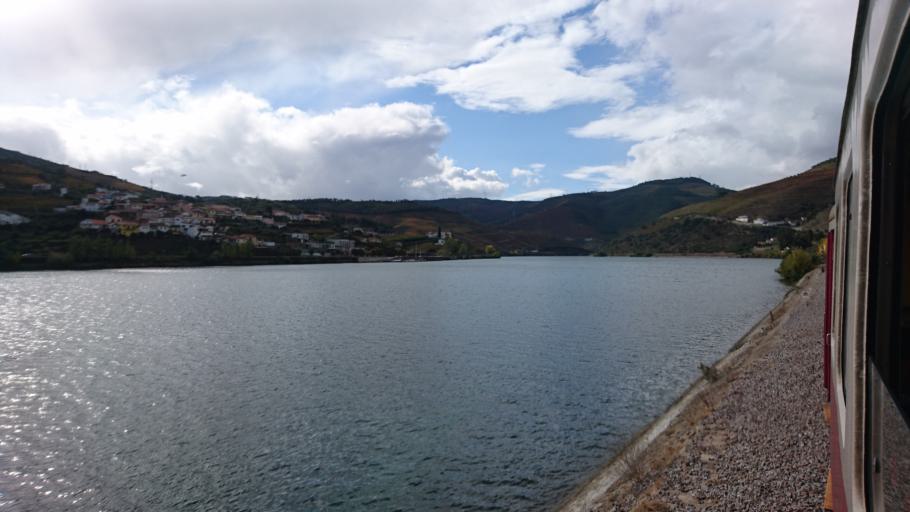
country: PT
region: Viseu
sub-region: Armamar
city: Armamar
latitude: 41.1561
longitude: -7.6789
